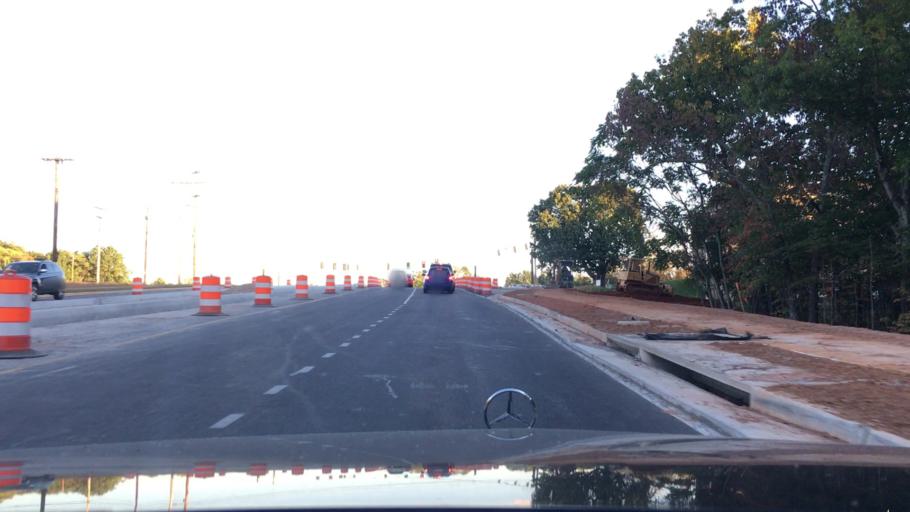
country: US
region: Virginia
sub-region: Campbell County
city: Timberlake
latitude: 37.3348
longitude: -79.2163
